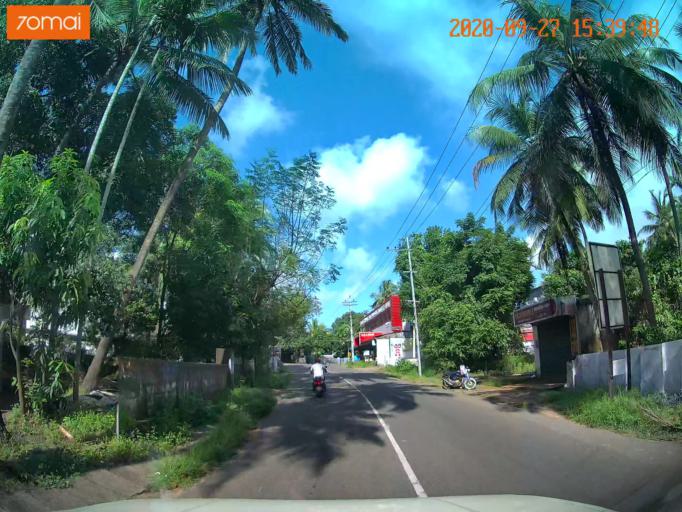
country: IN
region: Kerala
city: Chavakkad
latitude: 10.4697
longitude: 76.0831
